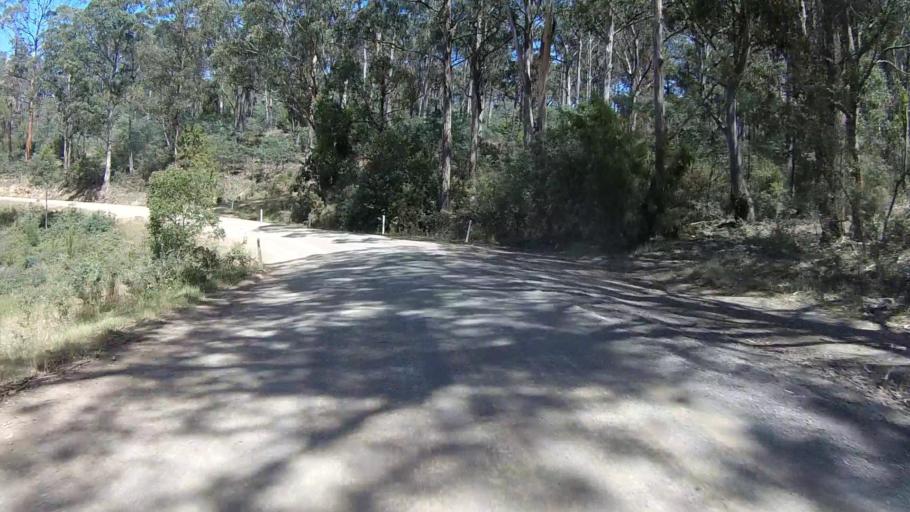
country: AU
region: Tasmania
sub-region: Sorell
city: Sorell
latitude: -42.7546
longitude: 147.6837
